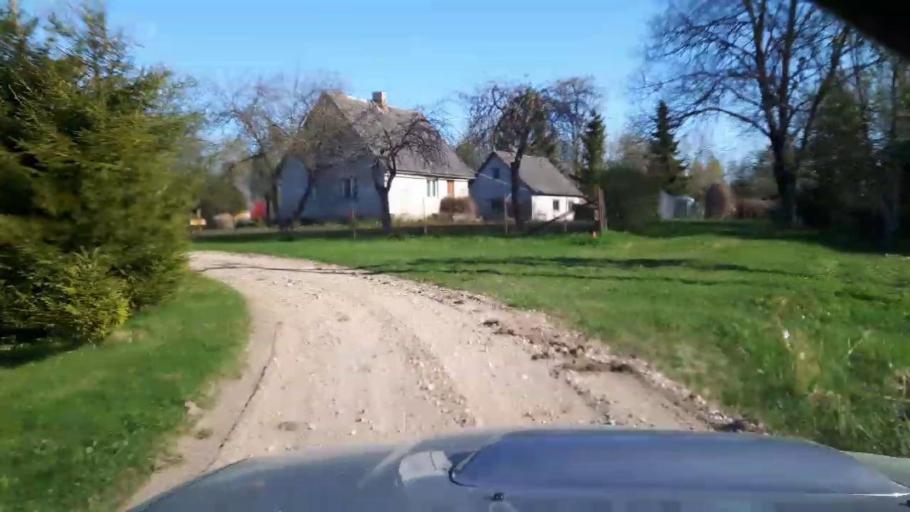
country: EE
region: Paernumaa
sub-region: Tootsi vald
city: Tootsi
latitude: 58.4827
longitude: 24.8255
